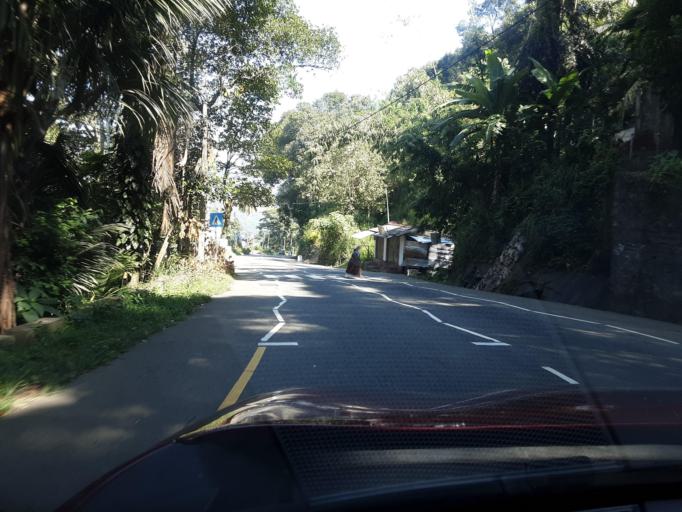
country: LK
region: Uva
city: Badulla
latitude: 7.0159
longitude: 81.0550
